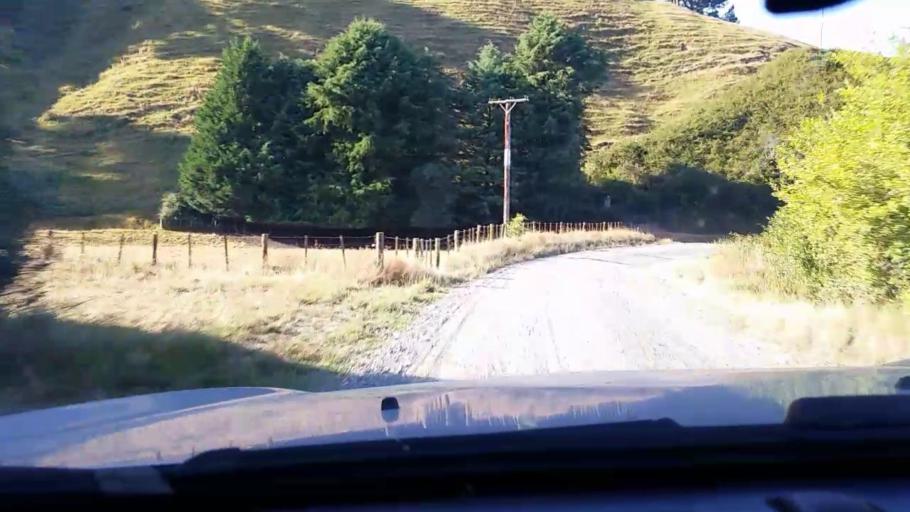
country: NZ
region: Waikato
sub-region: Taupo District
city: Taupo
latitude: -38.4797
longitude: 176.2169
